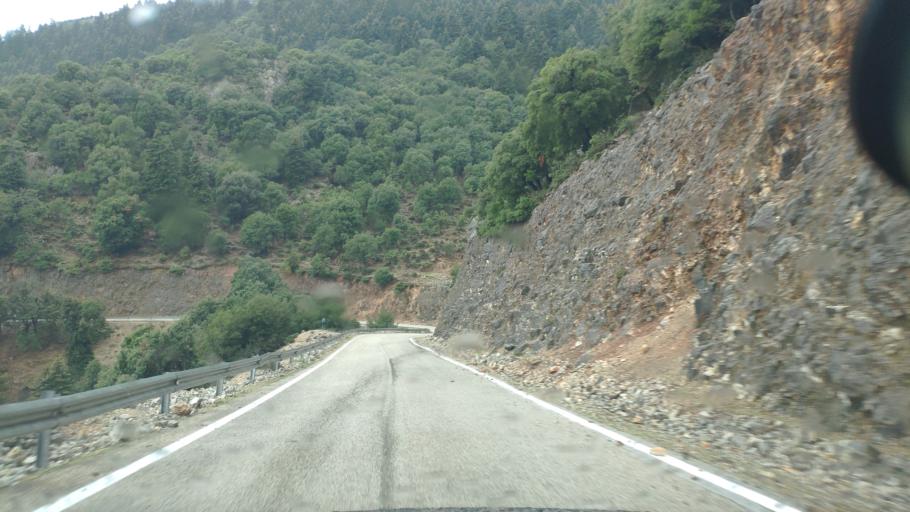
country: GR
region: West Greece
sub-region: Nomos Aitolias kai Akarnanias
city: Krikellos
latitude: 39.0338
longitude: 21.3670
